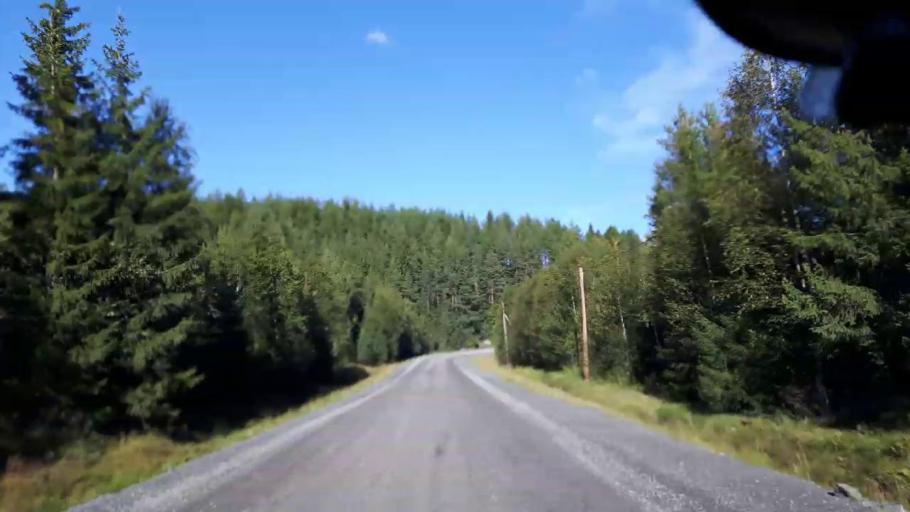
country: SE
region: Vaesternorrland
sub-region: Solleftea Kommun
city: As
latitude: 63.4580
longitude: 16.2502
